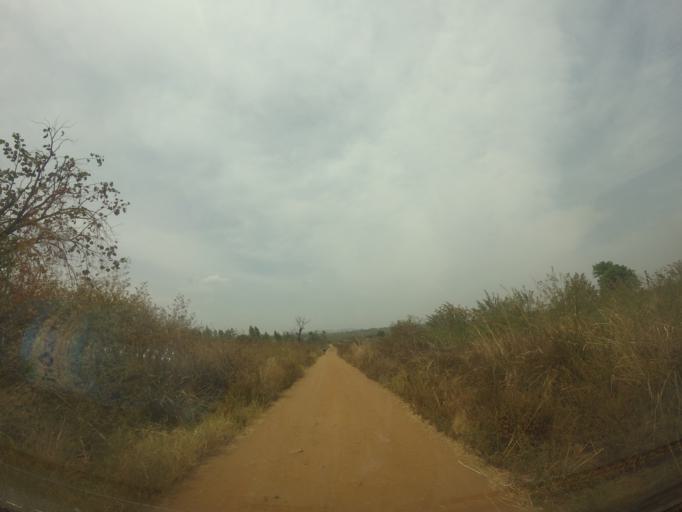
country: UG
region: Northern Region
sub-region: Nebbi District
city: Nebbi
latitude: 2.6243
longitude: 31.0396
